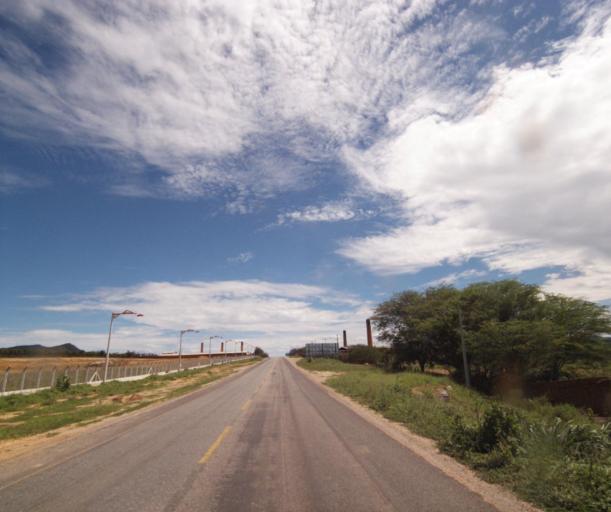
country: BR
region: Bahia
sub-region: Guanambi
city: Guanambi
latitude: -14.2598
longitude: -42.7824
